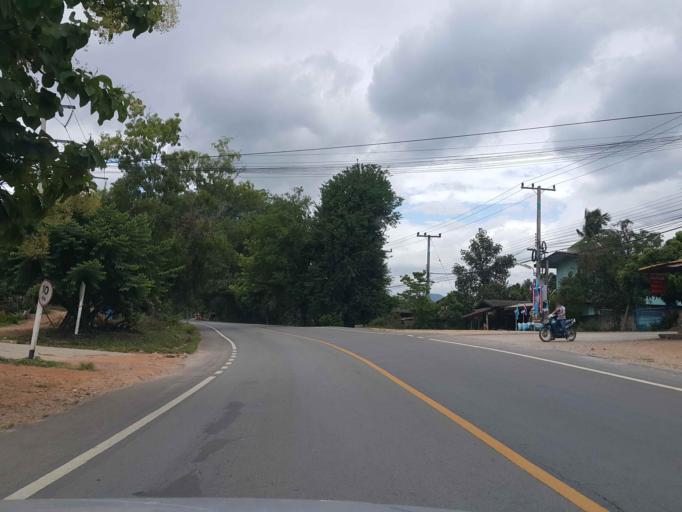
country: TH
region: Lamphun
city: Thung Hua Chang
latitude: 17.9710
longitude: 98.8842
